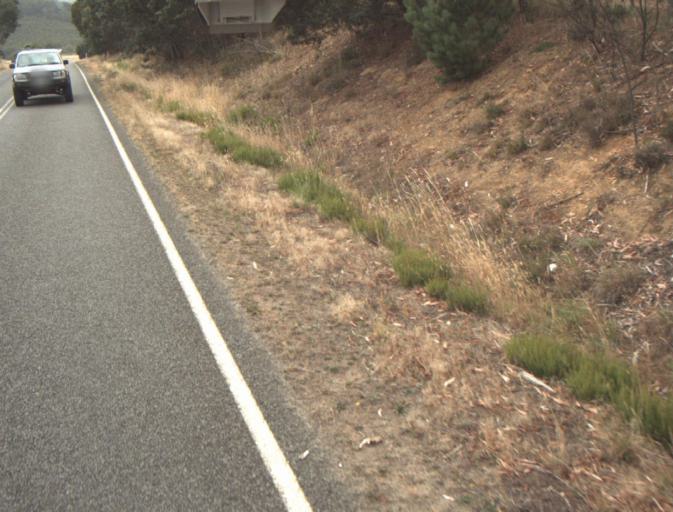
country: AU
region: Tasmania
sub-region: Northern Midlands
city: Evandale
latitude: -41.4735
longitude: 147.5437
